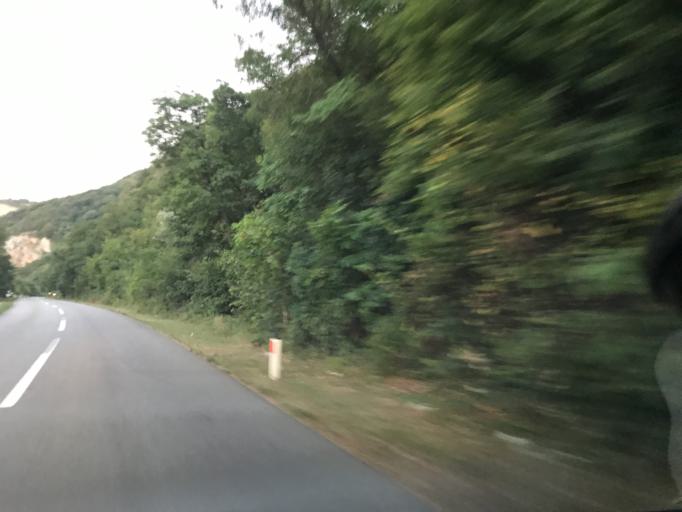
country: RO
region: Caras-Severin
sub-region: Comuna Pescari
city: Coronini
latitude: 44.6526
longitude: 21.7155
